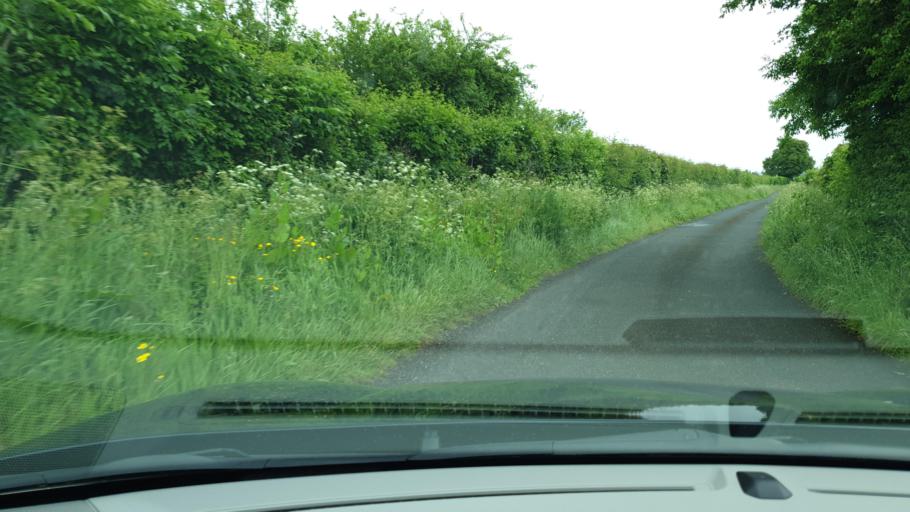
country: IE
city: Confey
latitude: 53.4259
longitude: -6.5337
